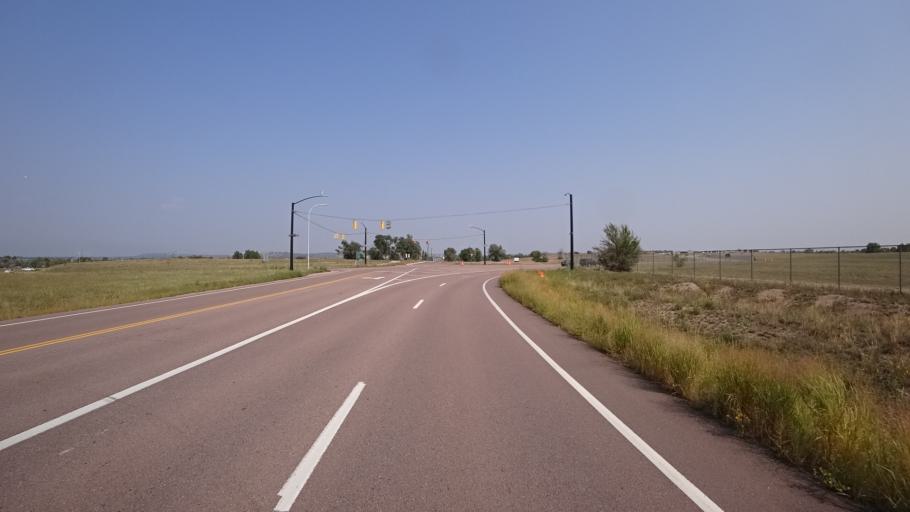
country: US
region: Colorado
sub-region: El Paso County
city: Cimarron Hills
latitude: 38.8269
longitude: -104.7202
